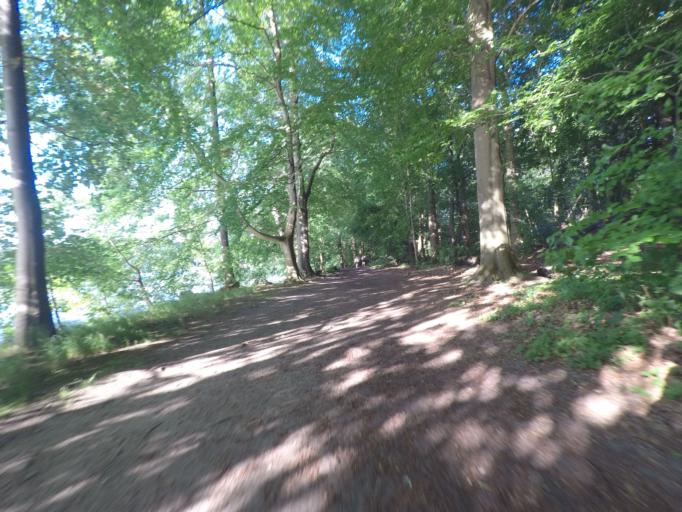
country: DE
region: Brandenburg
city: Joachimsthal
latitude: 52.9190
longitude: 13.7203
